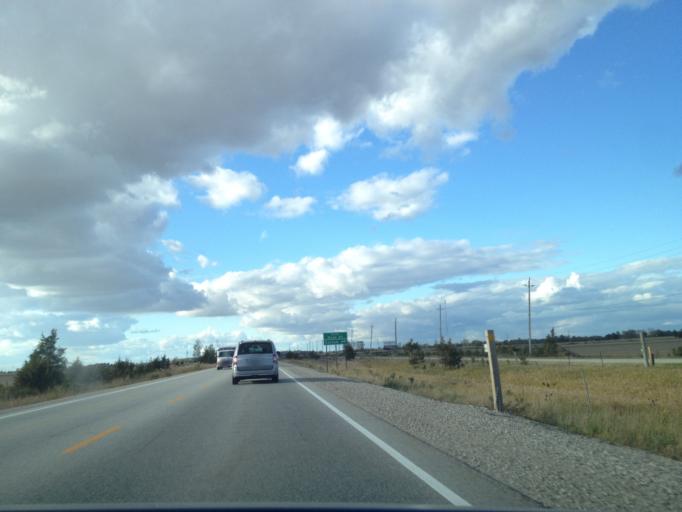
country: CA
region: Ontario
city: Amherstburg
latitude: 42.1161
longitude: -82.7521
